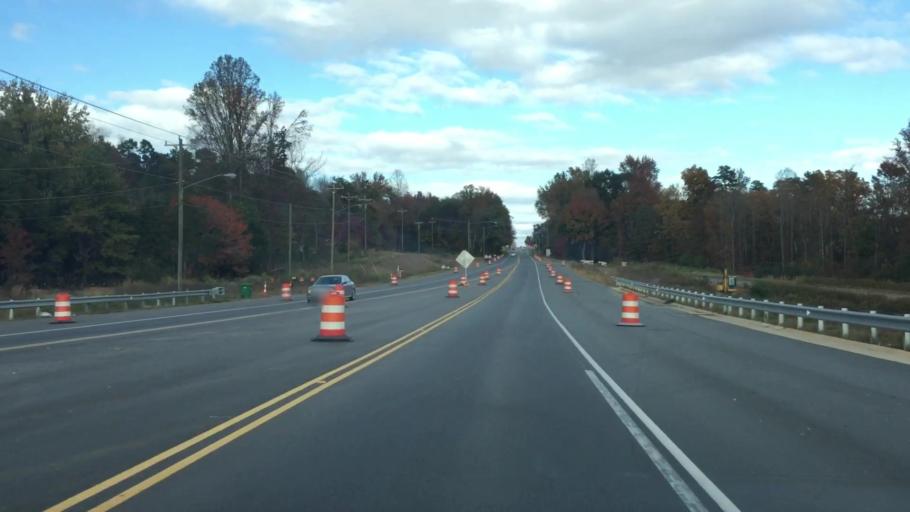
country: US
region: North Carolina
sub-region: Forsyth County
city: Walkertown
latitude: 36.1488
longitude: -80.1537
